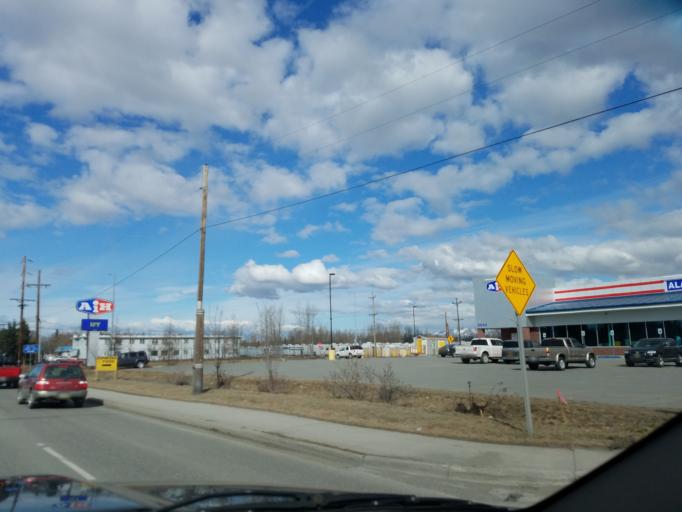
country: US
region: Alaska
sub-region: Anchorage Municipality
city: Anchorage
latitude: 61.1694
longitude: -149.8680
